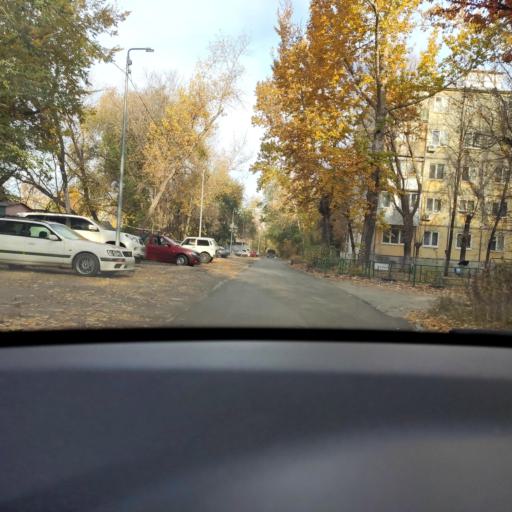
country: RU
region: Samara
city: Samara
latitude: 53.2169
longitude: 50.2065
